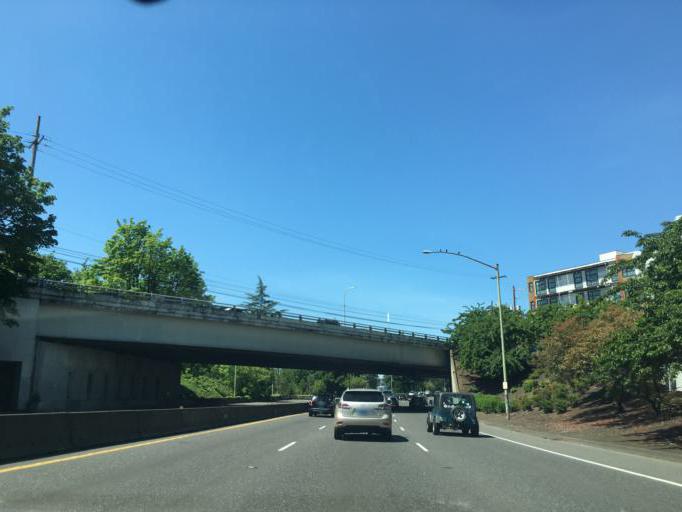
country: US
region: Oregon
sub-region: Clackamas County
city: Milwaukie
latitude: 45.4869
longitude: -122.6495
